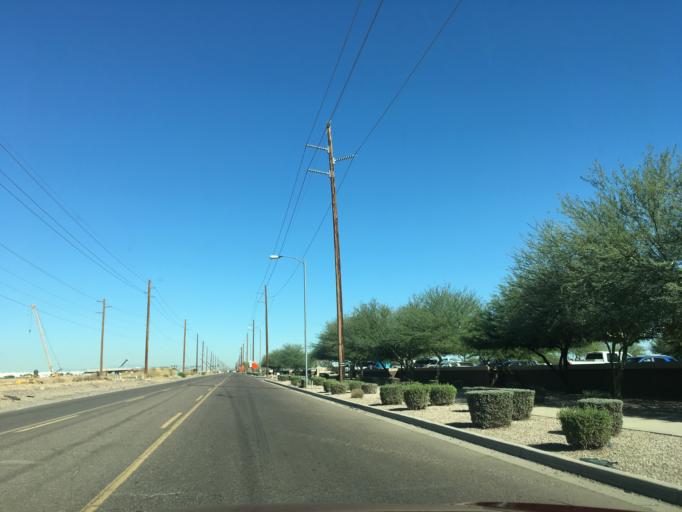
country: US
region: Arizona
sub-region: Maricopa County
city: Laveen
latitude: 33.4252
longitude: -112.1865
